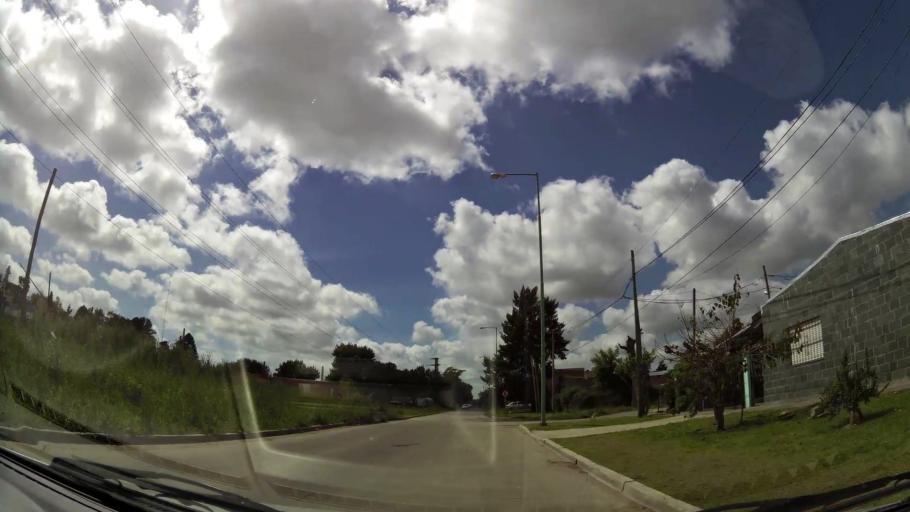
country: AR
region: Buenos Aires
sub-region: Partido de Quilmes
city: Quilmes
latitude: -34.8337
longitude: -58.1876
